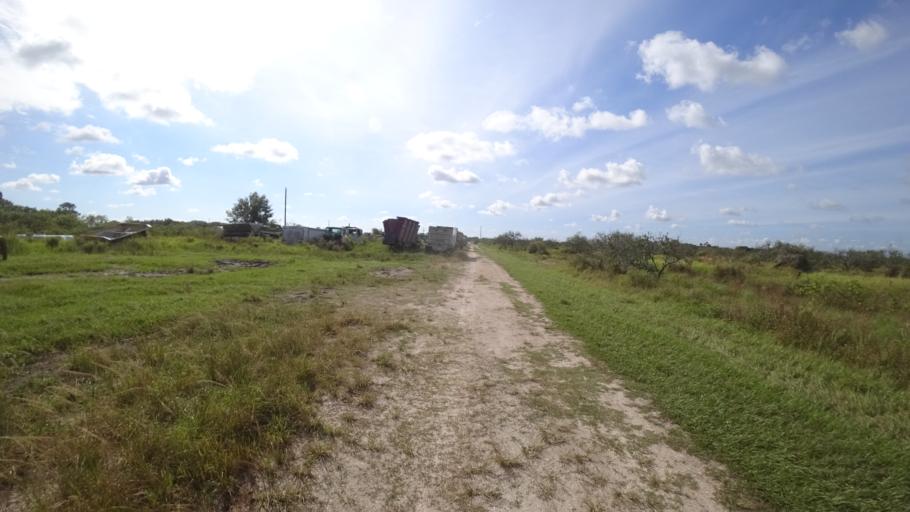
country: US
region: Florida
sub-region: Hillsborough County
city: Wimauma
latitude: 27.6076
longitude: -82.2880
